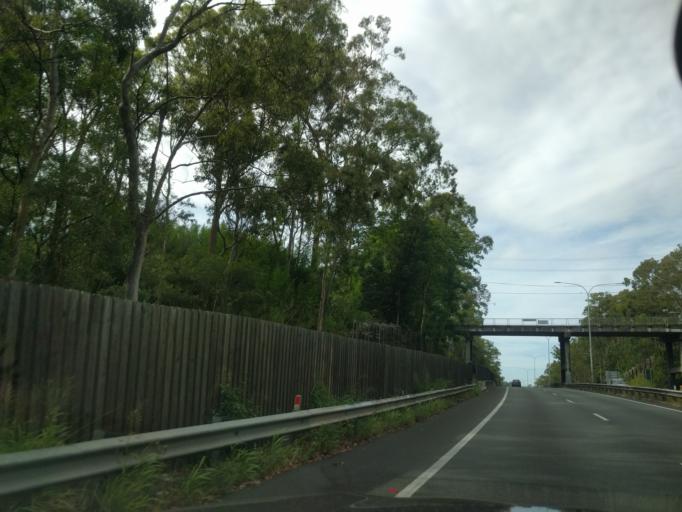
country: AU
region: Queensland
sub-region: Brisbane
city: Kenmore Hills
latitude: -27.5105
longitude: 152.9587
